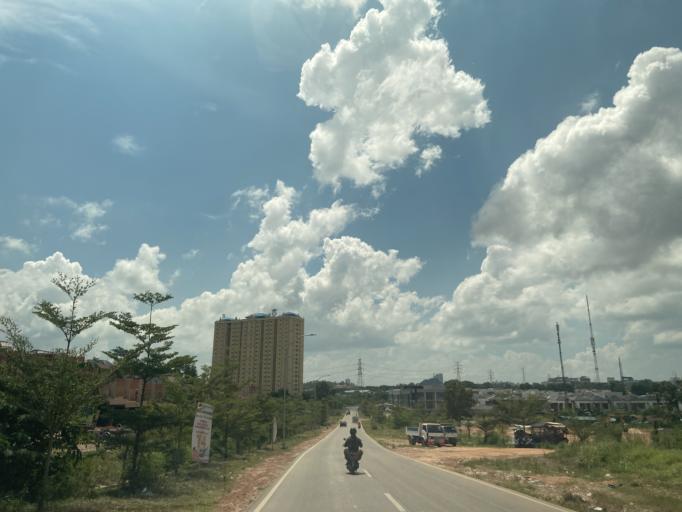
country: SG
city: Singapore
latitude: 1.1147
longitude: 104.0288
